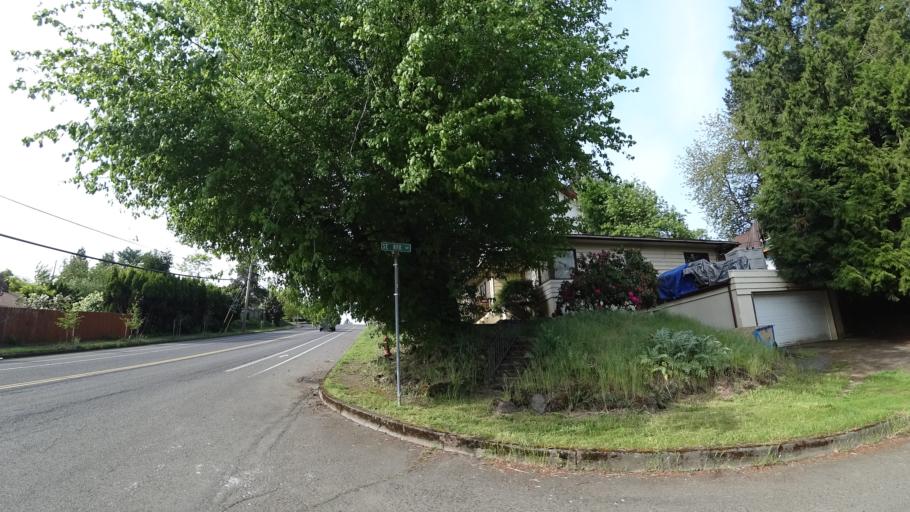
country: US
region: Oregon
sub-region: Clackamas County
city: Milwaukie
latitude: 45.4686
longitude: -122.6159
